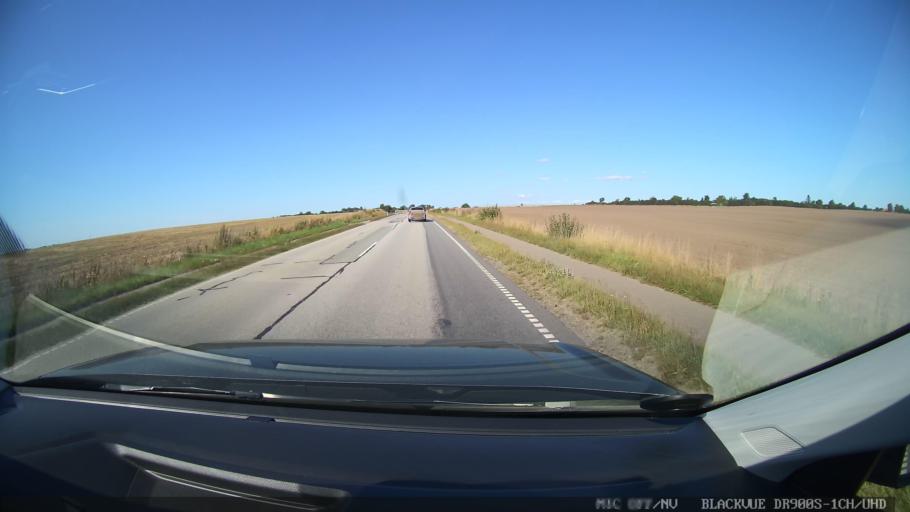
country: DK
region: Central Jutland
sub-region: Randers Kommune
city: Spentrup
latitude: 56.5165
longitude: 10.0155
